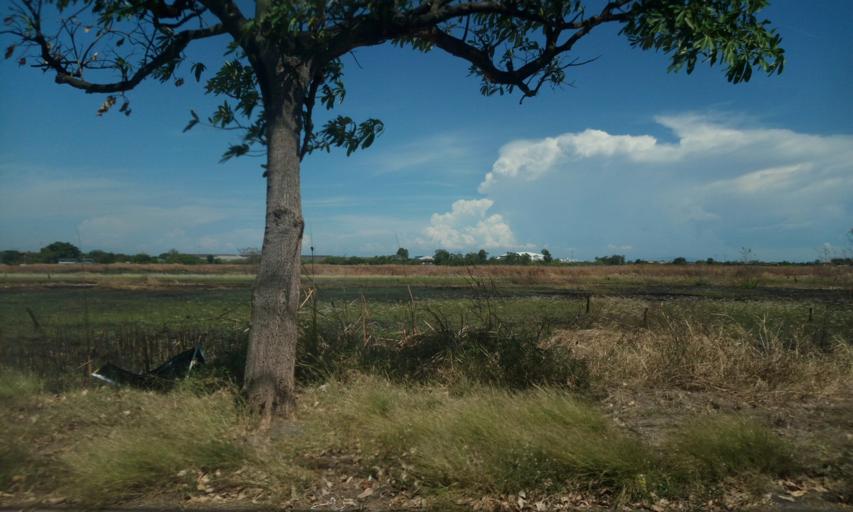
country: TH
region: Samut Prakan
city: Bang Bo District
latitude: 13.5923
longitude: 100.8044
